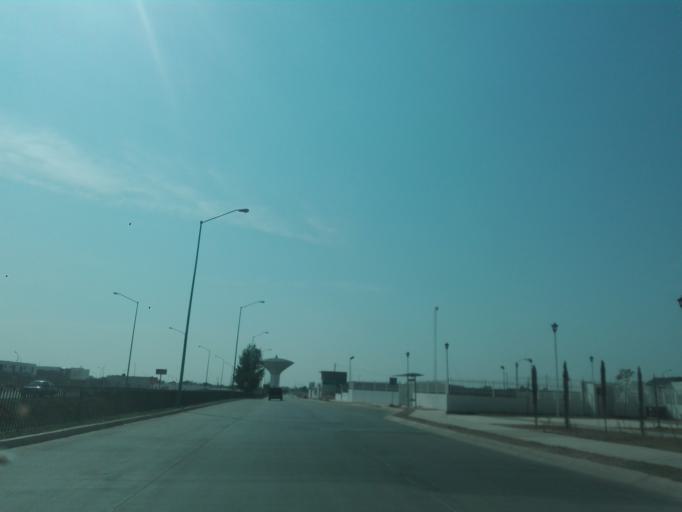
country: MX
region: Guanajuato
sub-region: Leon
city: Ladrilleras del Refugio
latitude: 21.0729
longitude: -101.5637
